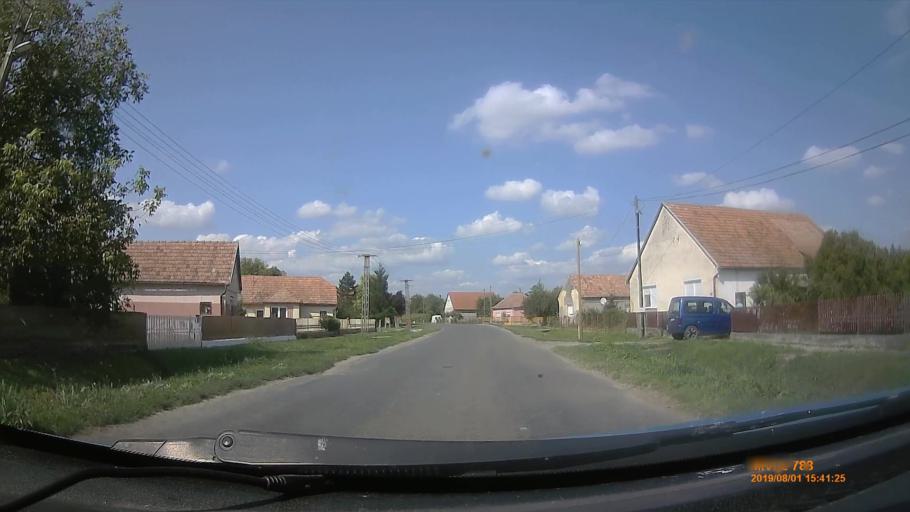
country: HU
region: Baranya
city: Szentlorinc
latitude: 45.9901
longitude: 17.9607
